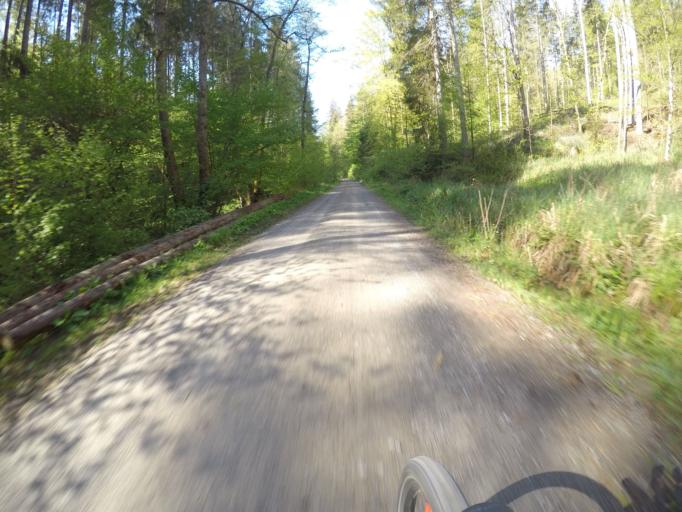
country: DE
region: Baden-Wuerttemberg
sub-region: Tuebingen Region
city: Tuebingen
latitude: 48.5543
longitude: 9.0811
